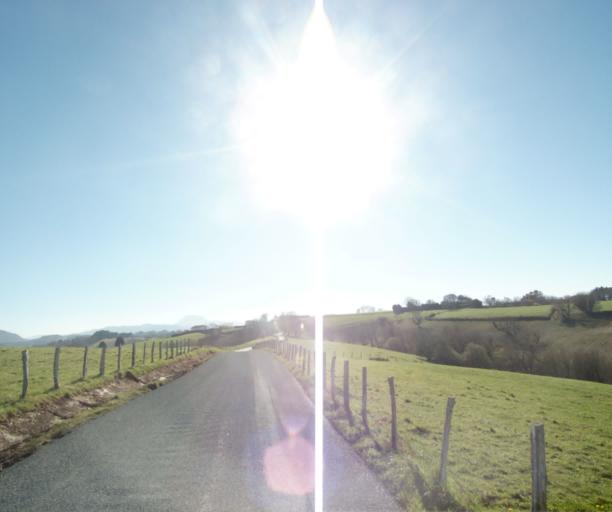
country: FR
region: Aquitaine
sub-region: Departement des Pyrenees-Atlantiques
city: Urrugne
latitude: 43.3730
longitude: -1.7229
